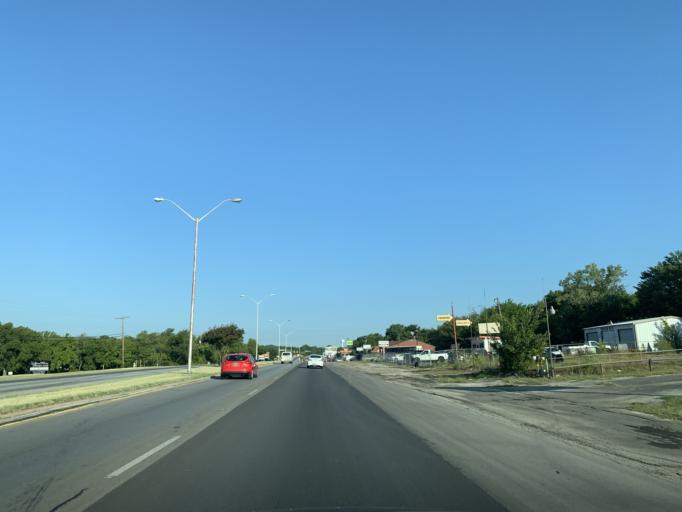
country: US
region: Texas
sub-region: Tarrant County
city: Sansom Park
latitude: 32.7950
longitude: -97.3952
